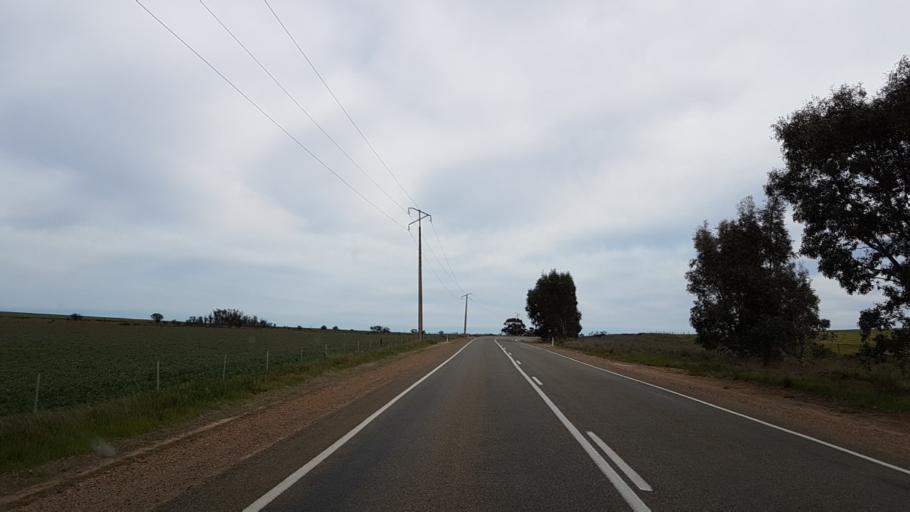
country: AU
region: South Australia
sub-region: Port Pirie City and Dists
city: Crystal Brook
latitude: -33.2773
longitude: 138.2991
